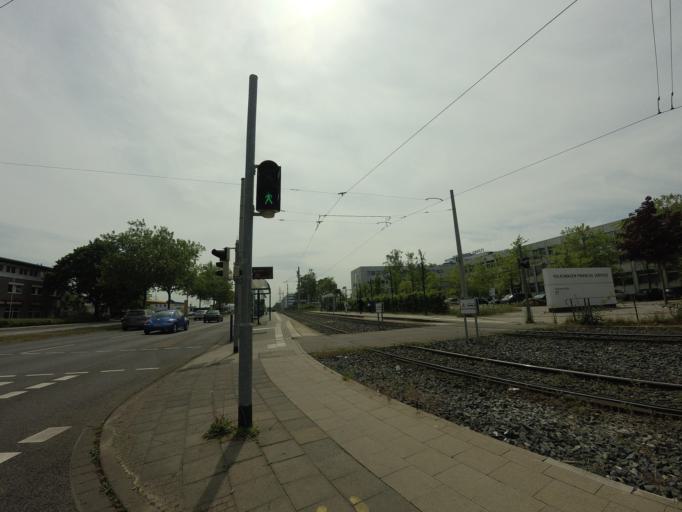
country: DE
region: Lower Saxony
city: Braunschweig
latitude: 52.3044
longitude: 10.5158
